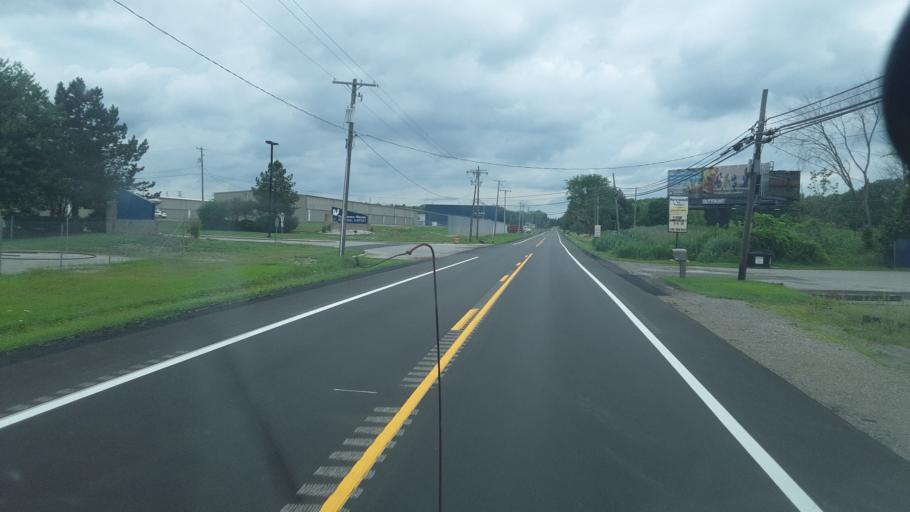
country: US
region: Ohio
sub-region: Trumbull County
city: Howland Center
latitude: 41.2569
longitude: -80.6638
